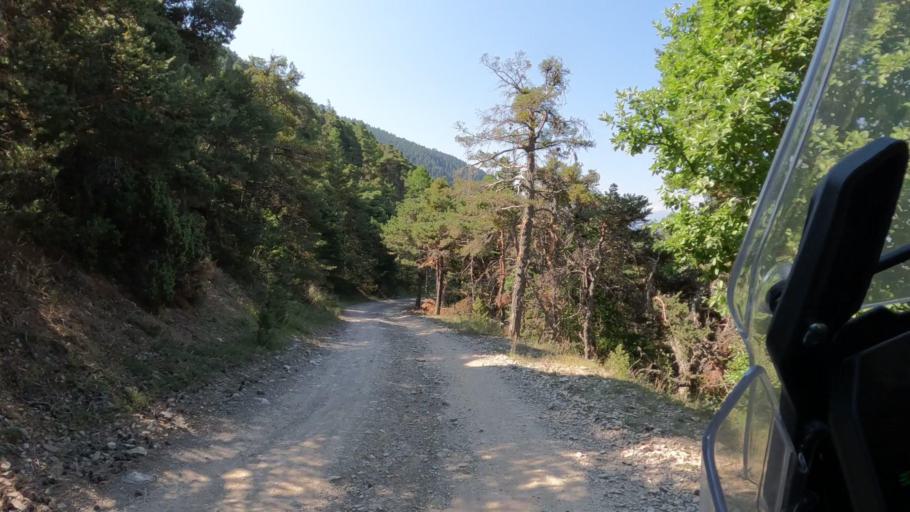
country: FR
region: Provence-Alpes-Cote d'Azur
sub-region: Departement des Hautes-Alpes
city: Embrun
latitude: 44.5883
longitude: 6.5537
